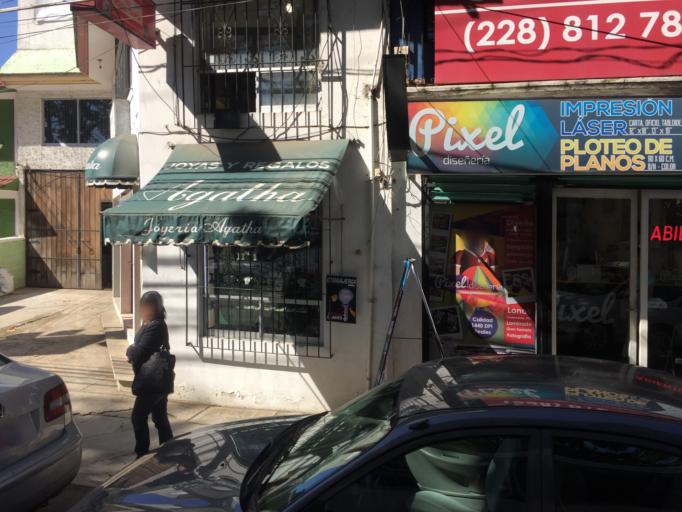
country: MX
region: Veracruz
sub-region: Xalapa
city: Xalapa de Enriquez
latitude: 19.5282
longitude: -96.8953
